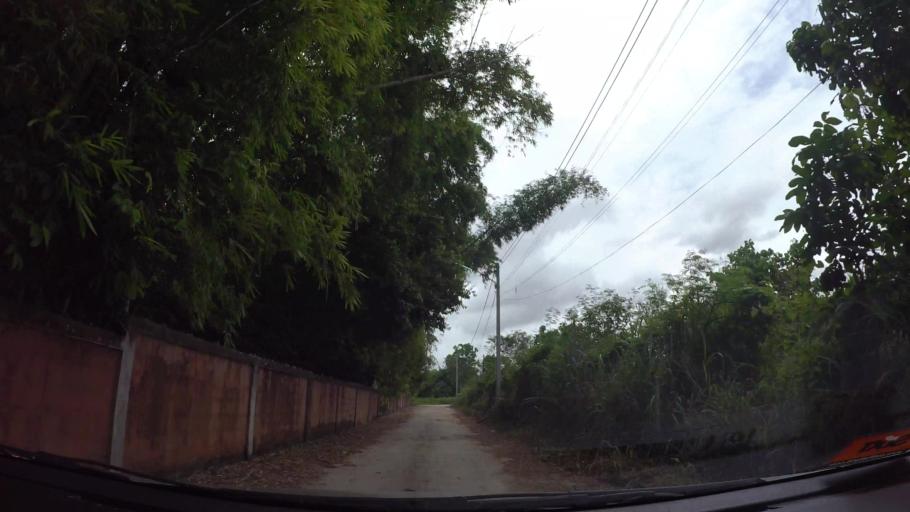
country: TH
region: Chon Buri
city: Si Racha
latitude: 13.1634
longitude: 100.9728
